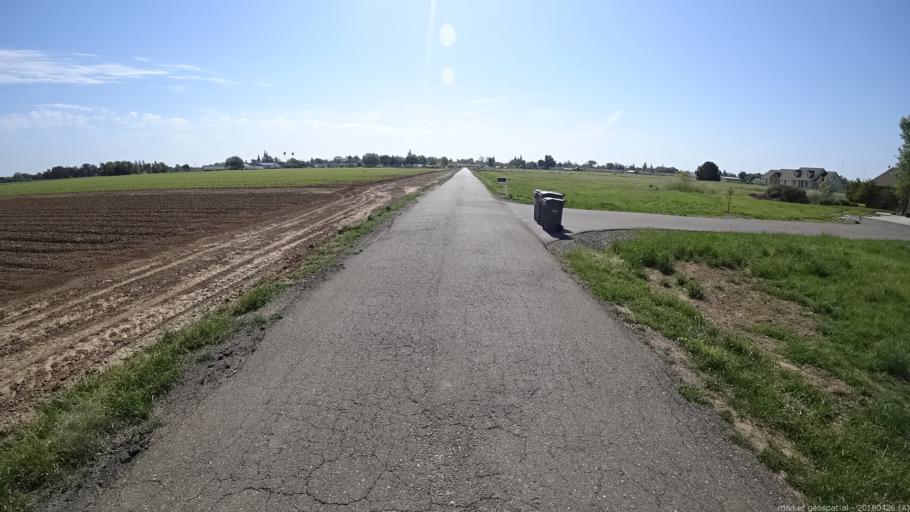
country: US
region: California
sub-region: Yolo County
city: West Sacramento
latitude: 38.5116
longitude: -121.5632
